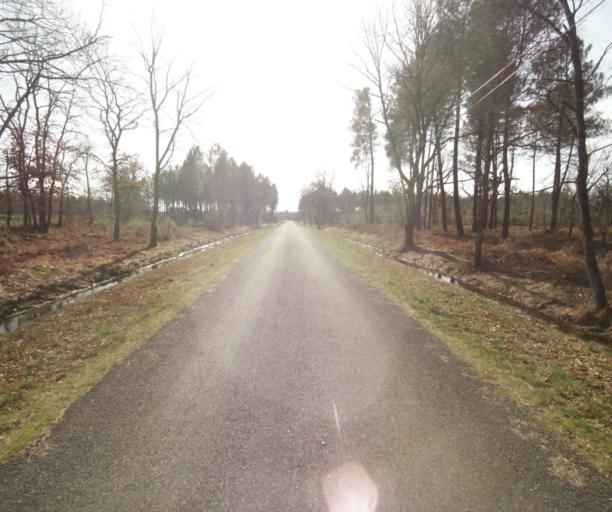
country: FR
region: Aquitaine
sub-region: Departement des Landes
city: Roquefort
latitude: 44.1338
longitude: -0.1879
